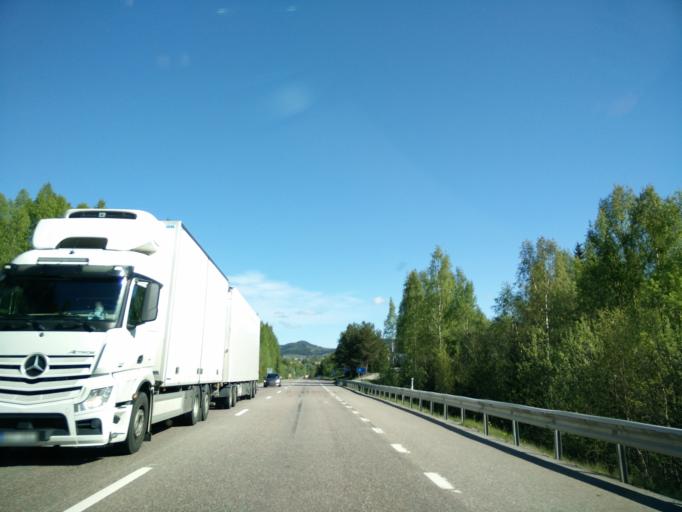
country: SE
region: Vaesternorrland
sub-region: Kramfors Kommun
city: Nordingra
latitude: 63.0401
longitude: 18.3267
